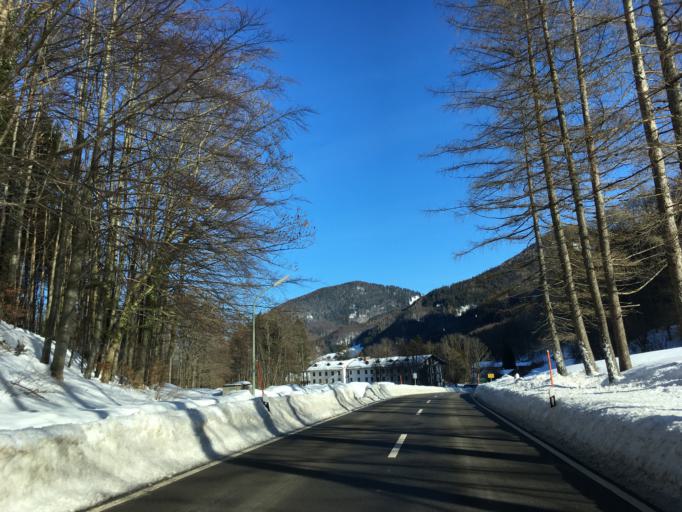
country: DE
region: Bavaria
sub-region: Upper Bavaria
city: Aschau im Chiemgau
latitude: 47.7581
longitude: 12.3206
